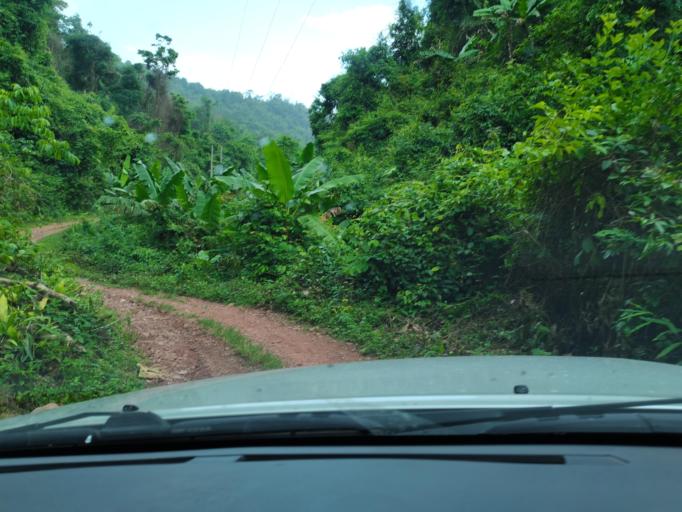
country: LA
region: Loungnamtha
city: Muang Nale
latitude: 20.5169
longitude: 101.0712
